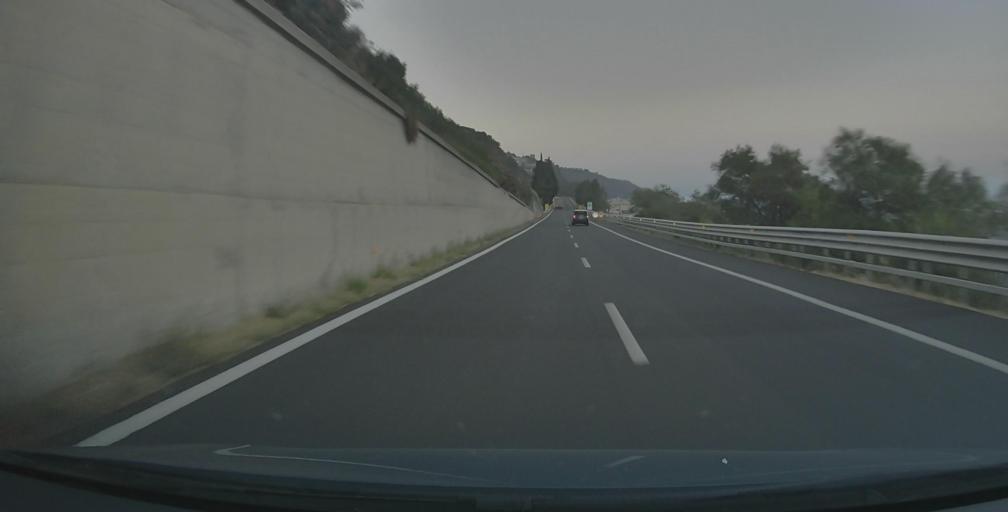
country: IT
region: Sicily
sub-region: Messina
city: Guidomandri Marina
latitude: 38.0319
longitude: 15.4471
